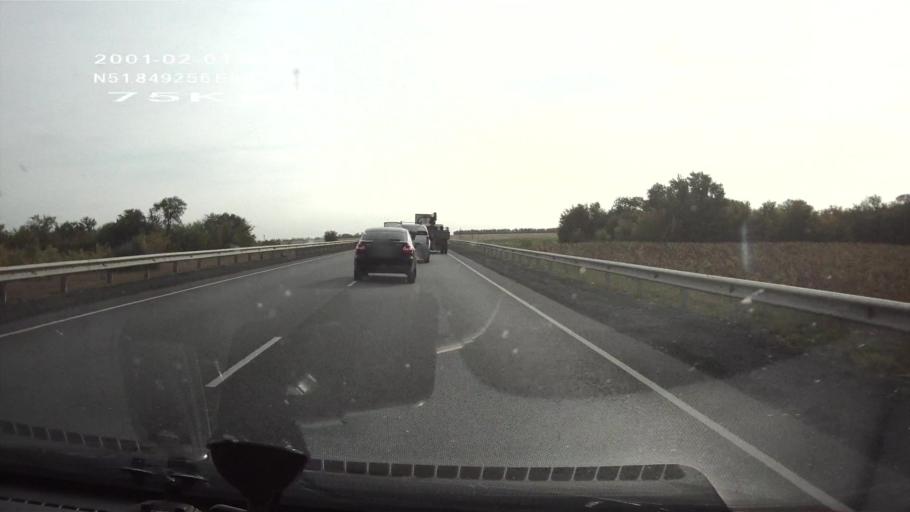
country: RU
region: Saratov
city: Yelshanka
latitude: 51.8490
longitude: 46.4866
